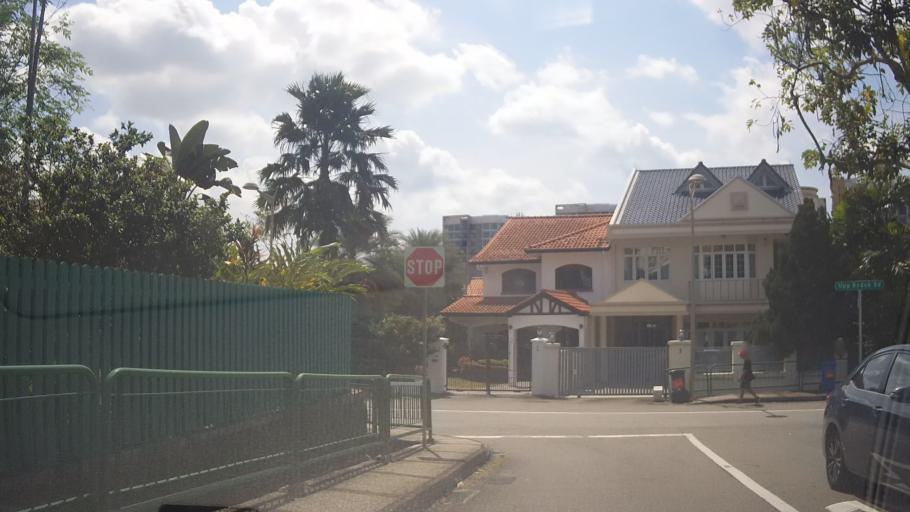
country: SG
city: Singapore
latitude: 1.3297
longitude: 103.9478
